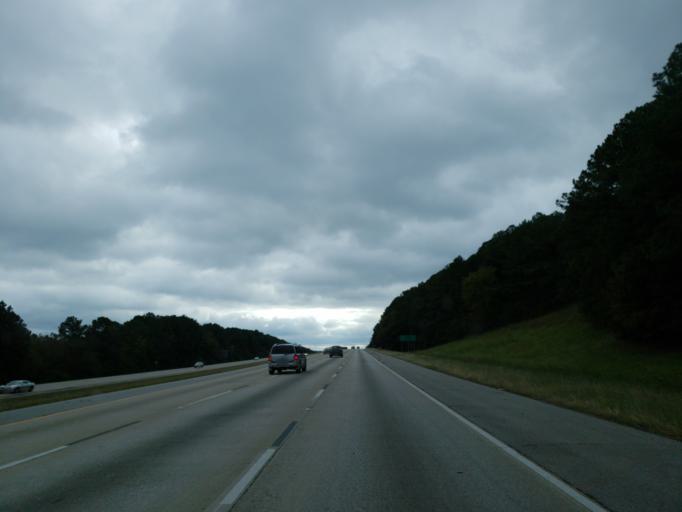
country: US
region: Alabama
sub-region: Jefferson County
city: Cahaba Heights
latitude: 33.4301
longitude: -86.7431
